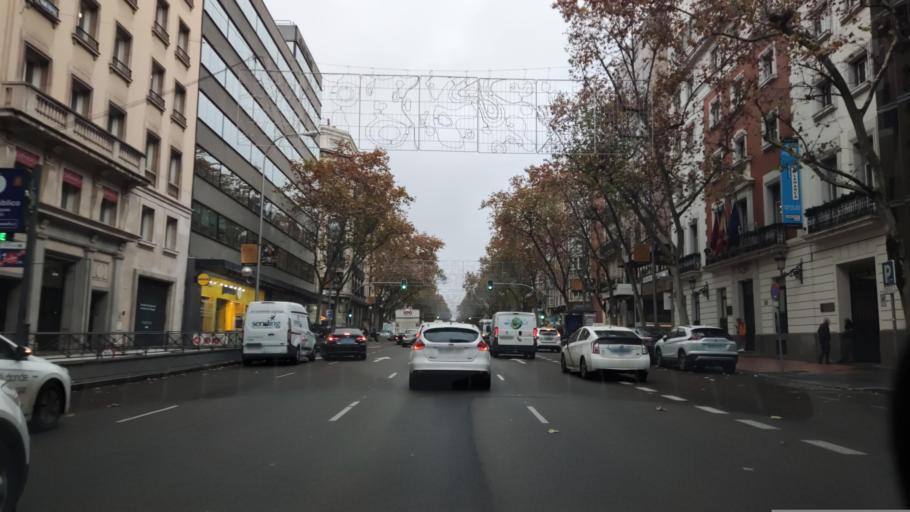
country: ES
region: Madrid
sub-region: Provincia de Madrid
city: Salamanca
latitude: 40.4270
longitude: -3.6840
